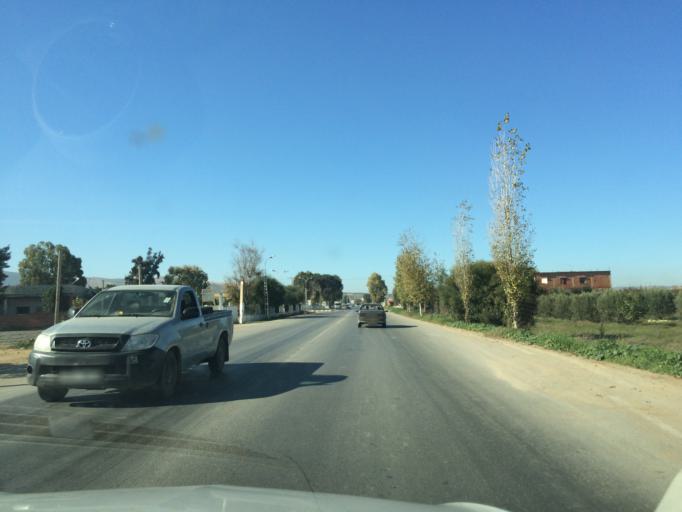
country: DZ
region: Relizane
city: Relizane
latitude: 35.9003
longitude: 0.5307
